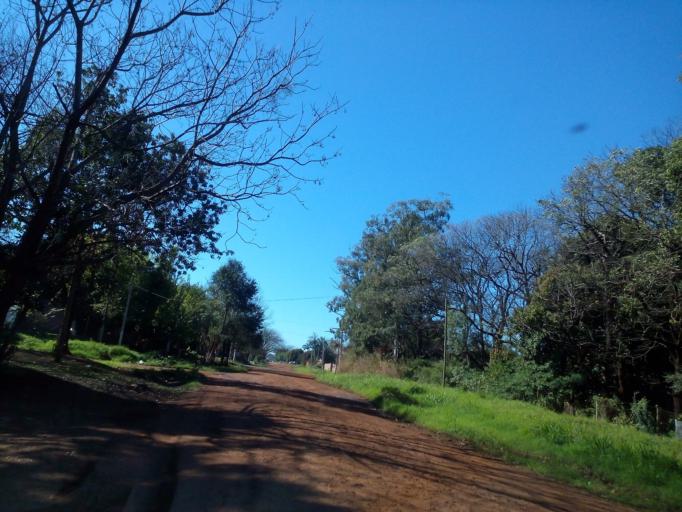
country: AR
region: Misiones
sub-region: Departamento de Capital
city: Posadas
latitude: -27.3908
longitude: -55.9327
